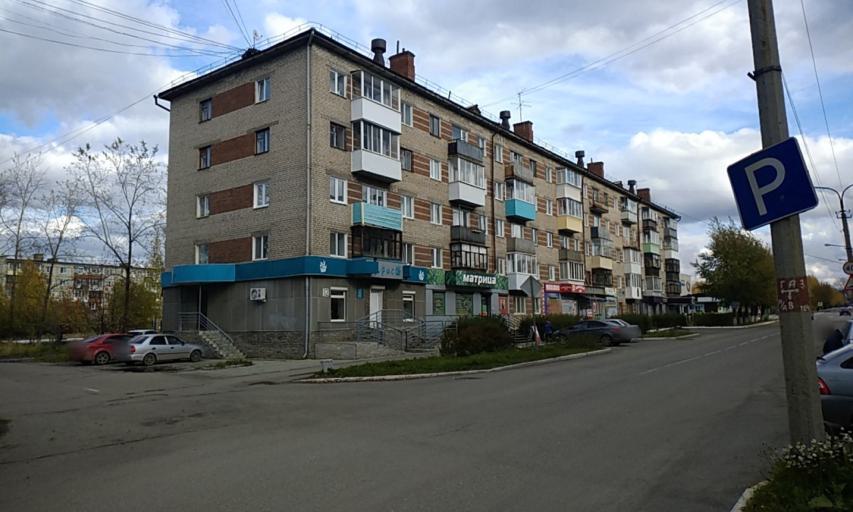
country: RU
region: Sverdlovsk
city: Krasnoural'sk
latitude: 58.3557
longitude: 60.0441
